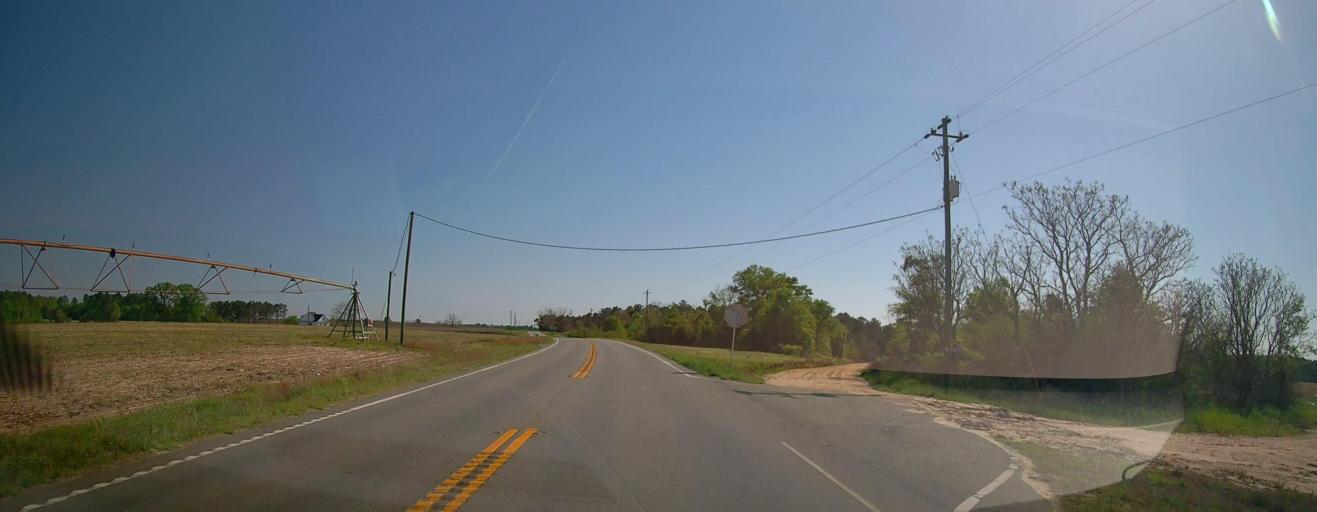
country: US
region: Georgia
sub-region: Pulaski County
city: Hawkinsville
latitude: 32.2021
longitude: -83.4953
